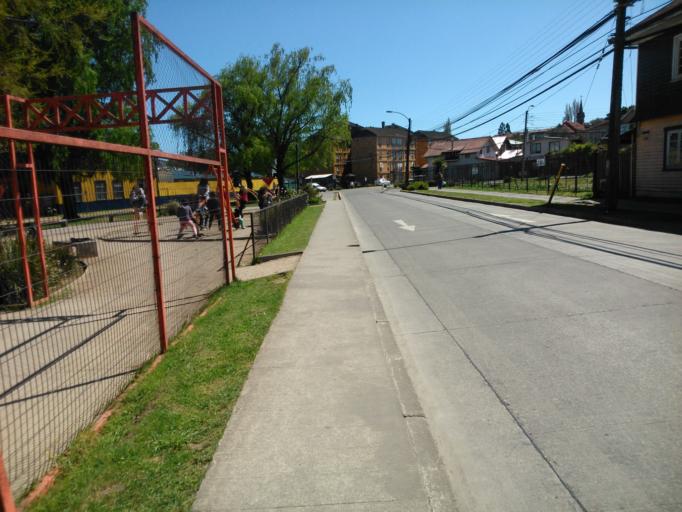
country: CL
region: Los Rios
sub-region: Provincia de Valdivia
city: Valdivia
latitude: -39.8208
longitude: -73.2476
